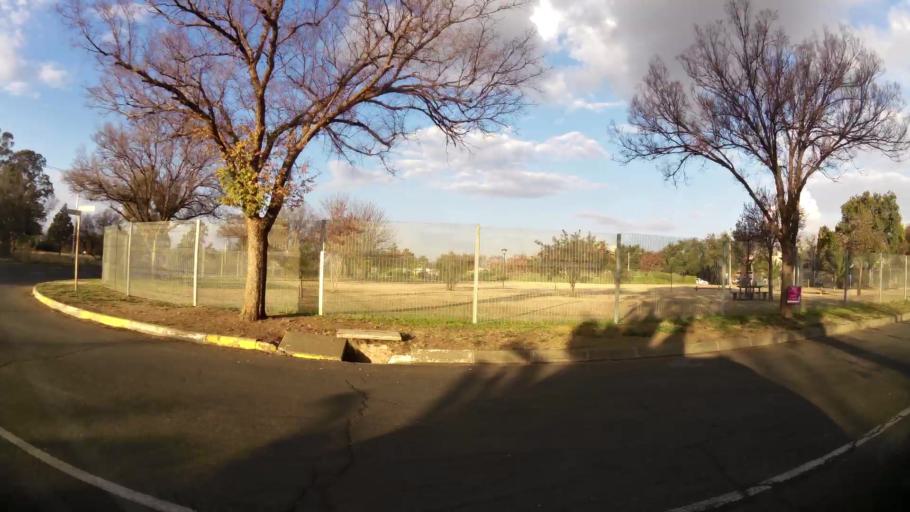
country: ZA
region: Orange Free State
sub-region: Mangaung Metropolitan Municipality
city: Bloemfontein
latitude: -29.1339
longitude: 26.1925
